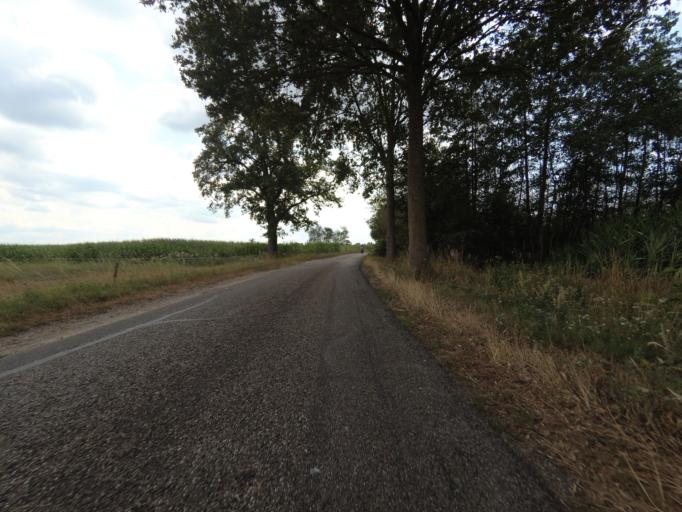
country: NL
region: Gelderland
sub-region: Berkelland
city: Eibergen
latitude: 52.1509
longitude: 6.6757
